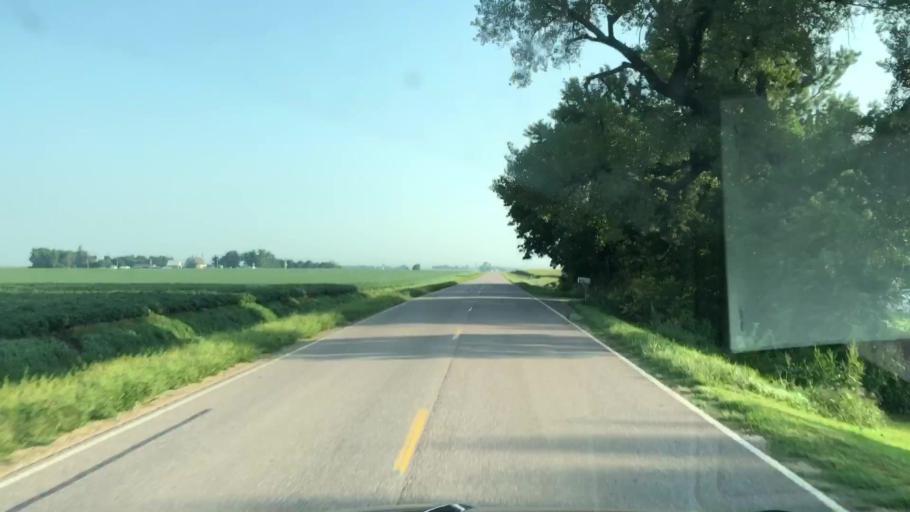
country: US
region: Iowa
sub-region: Sioux County
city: Hull
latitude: 43.2084
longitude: -96.0007
